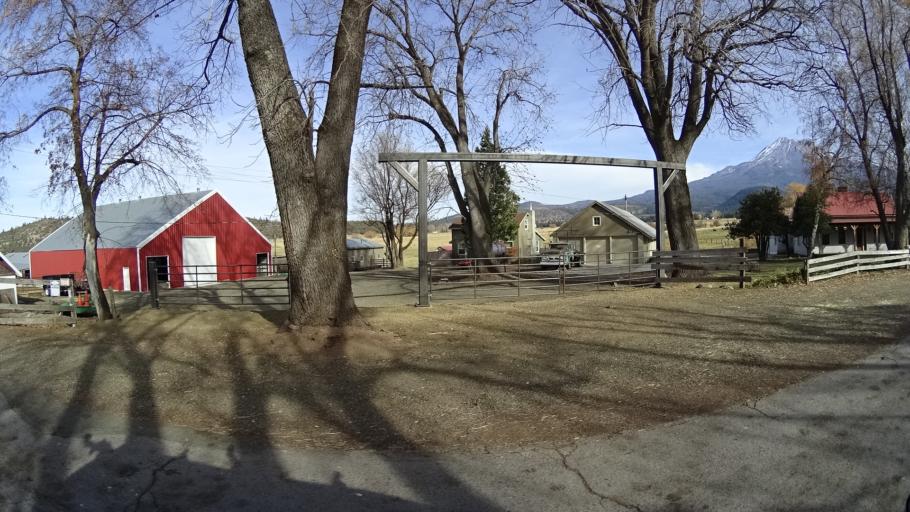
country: US
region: California
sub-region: Siskiyou County
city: Weed
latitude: 41.4557
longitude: -122.3841
